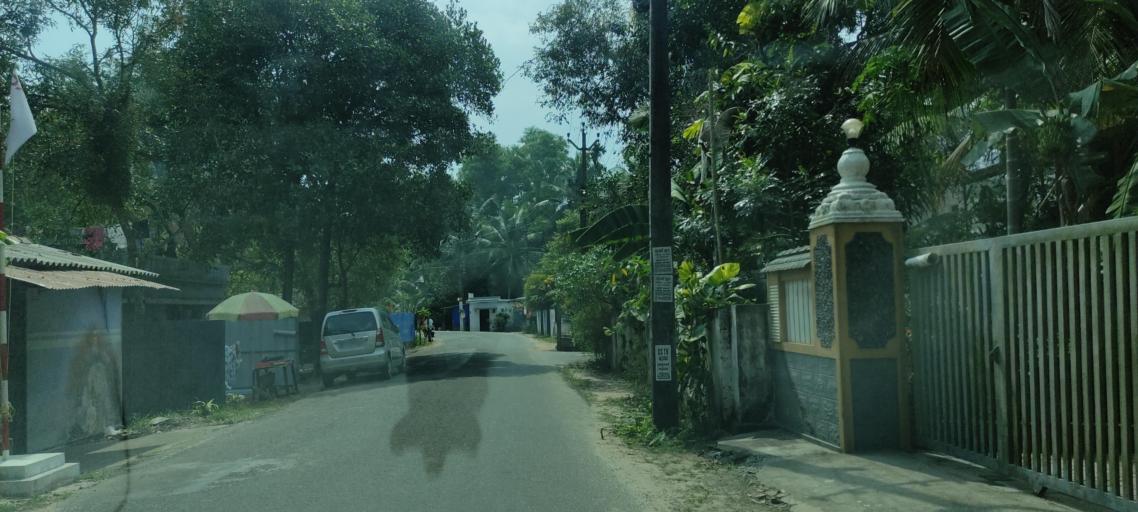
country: IN
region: Kerala
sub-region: Alappuzha
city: Shertallai
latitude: 9.6142
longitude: 76.3471
